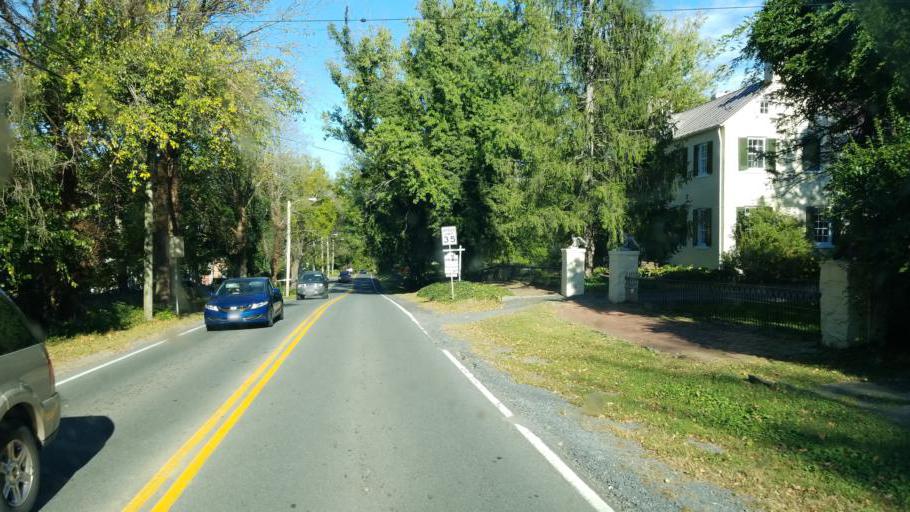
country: US
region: Virginia
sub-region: Prince William County
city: Bull Run Mountain Estates
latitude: 38.9706
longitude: -77.7314
